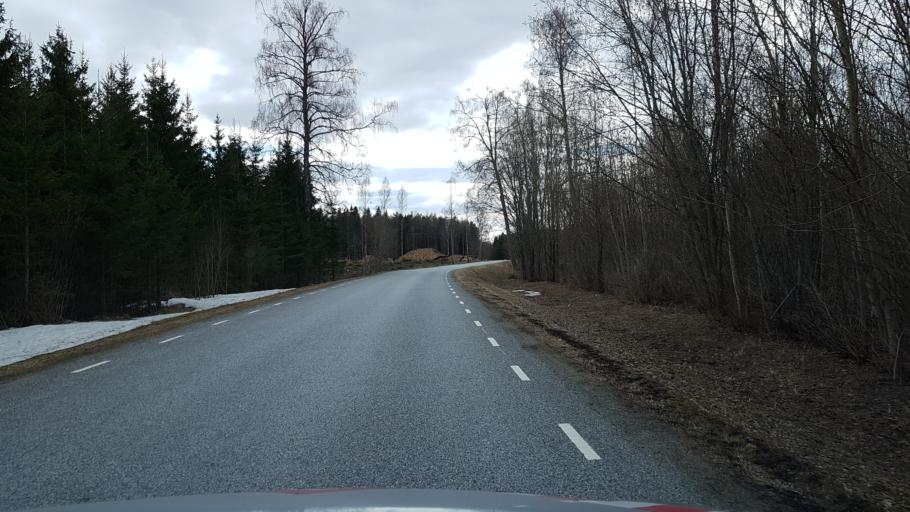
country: EE
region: Laeaene-Virumaa
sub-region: Tamsalu vald
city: Tamsalu
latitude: 59.2225
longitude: 26.1625
